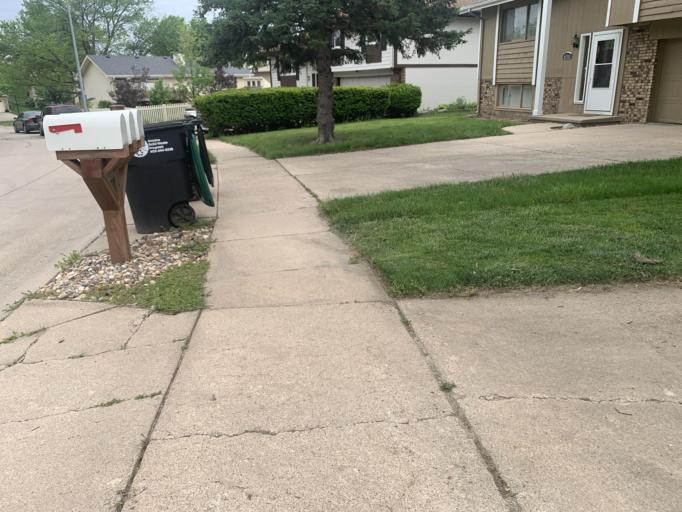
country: US
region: Nebraska
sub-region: Douglas County
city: Ralston
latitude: 41.1921
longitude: -96.0854
